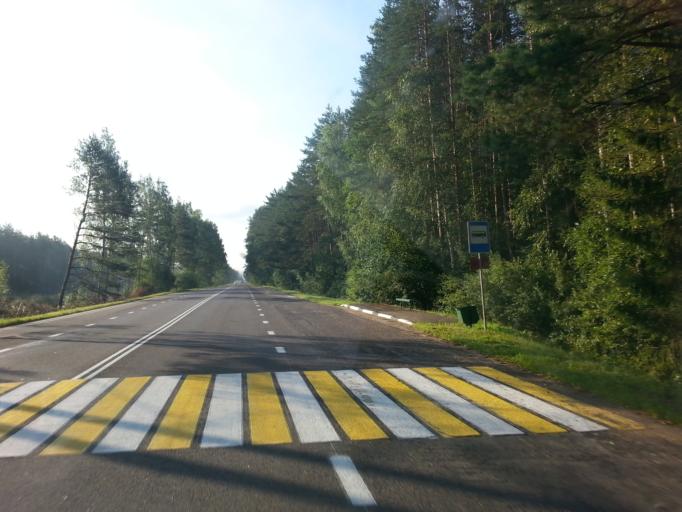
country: BY
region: Minsk
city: Kryvichy
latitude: 54.7494
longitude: 27.1148
